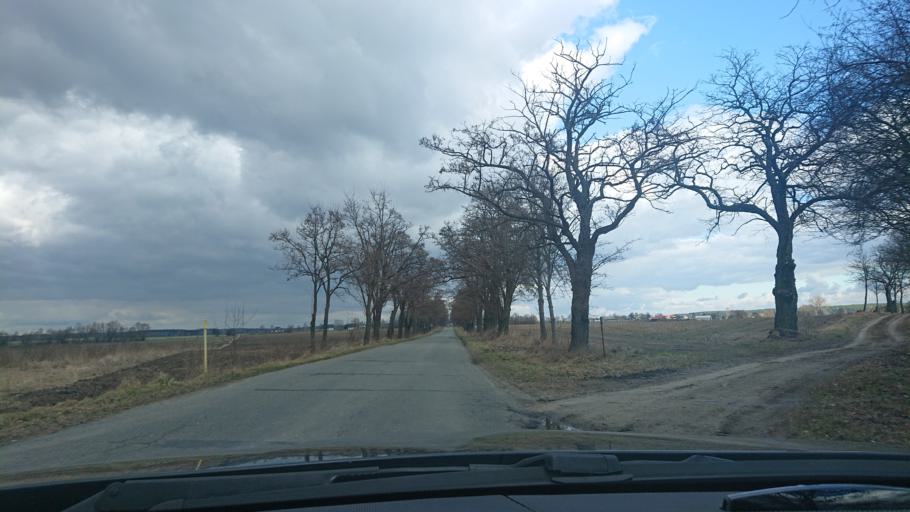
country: PL
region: Greater Poland Voivodeship
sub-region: Powiat gnieznienski
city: Niechanowo
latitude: 52.5746
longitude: 17.7058
